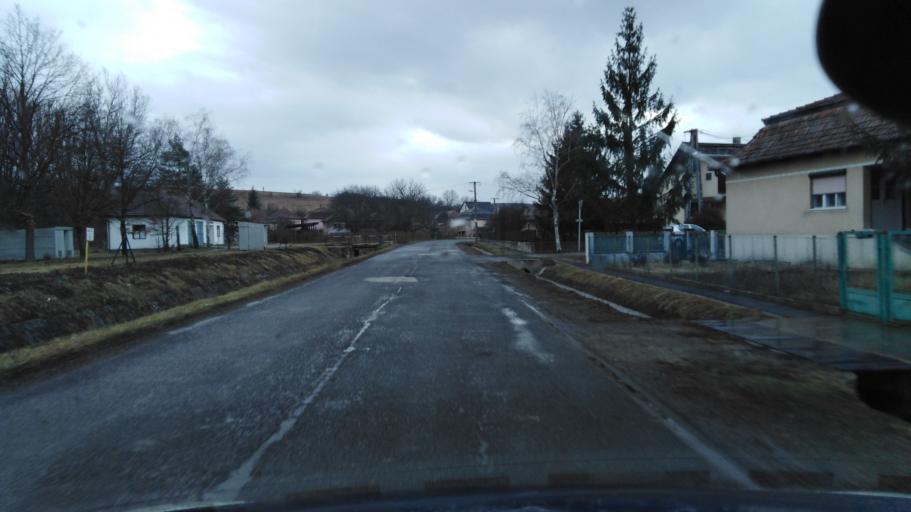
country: HU
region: Nograd
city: Karancskeszi
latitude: 48.1795
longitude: 19.6509
